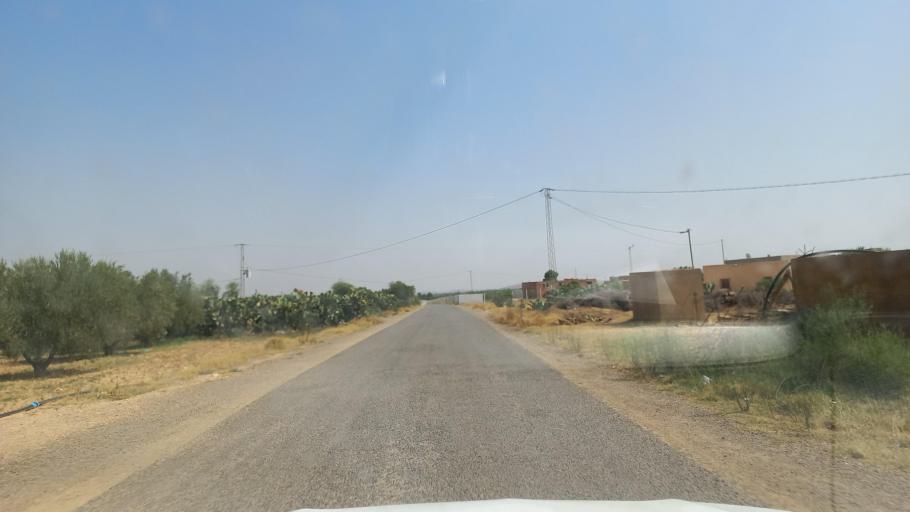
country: TN
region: Al Qasrayn
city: Kasserine
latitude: 35.2444
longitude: 9.0259
